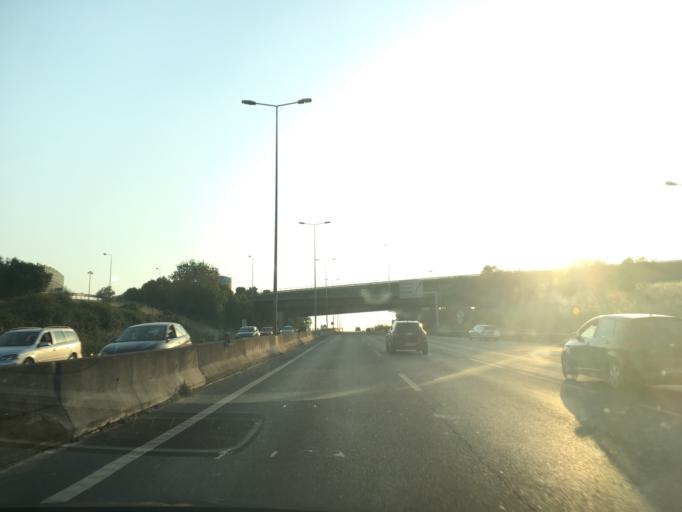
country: PT
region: Lisbon
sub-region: Oeiras
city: Barcarena
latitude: 38.7478
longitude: -9.2714
